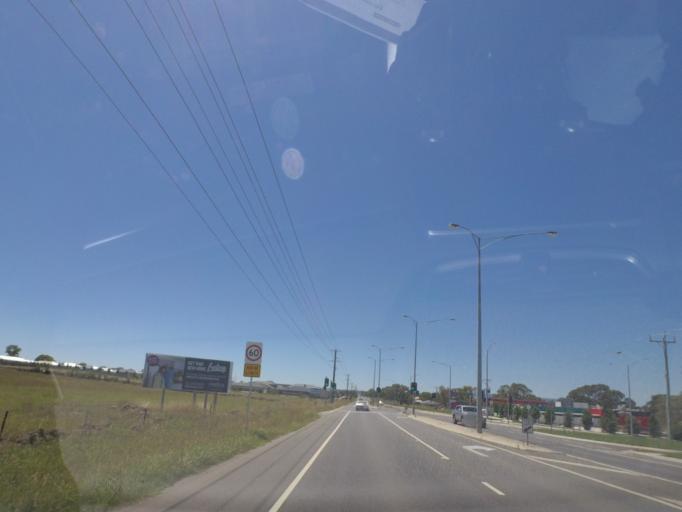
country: AU
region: Victoria
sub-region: Whittlesea
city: Epping
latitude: -37.6165
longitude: 145.0299
